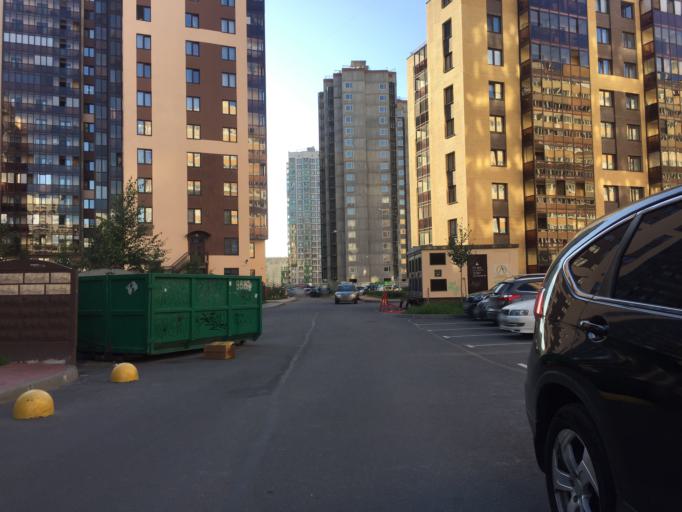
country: RU
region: Leningrad
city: Murino
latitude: 60.0545
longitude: 30.4316
